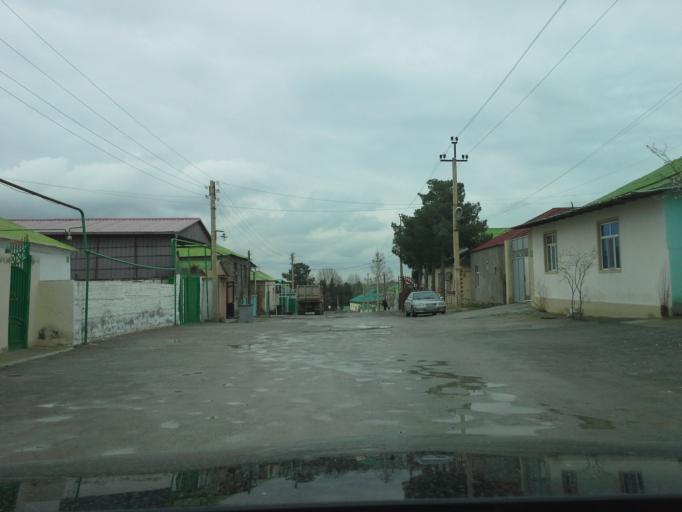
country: TM
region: Ahal
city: Abadan
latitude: 37.9599
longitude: 58.2199
